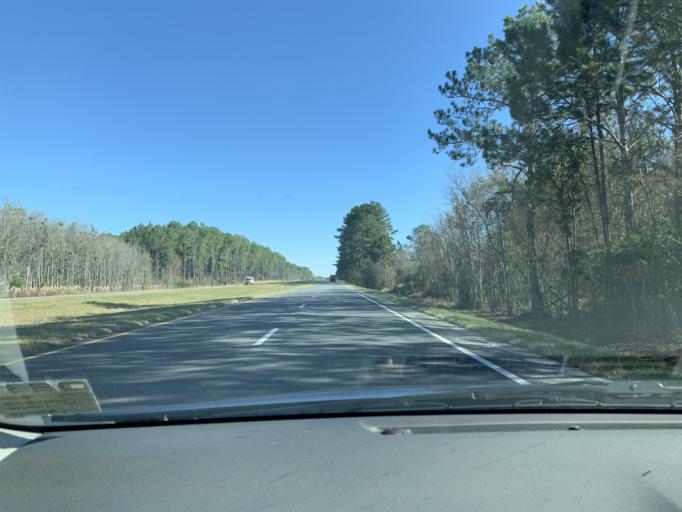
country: US
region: Georgia
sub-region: Atkinson County
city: Willacoochee
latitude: 31.3308
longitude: -83.0131
